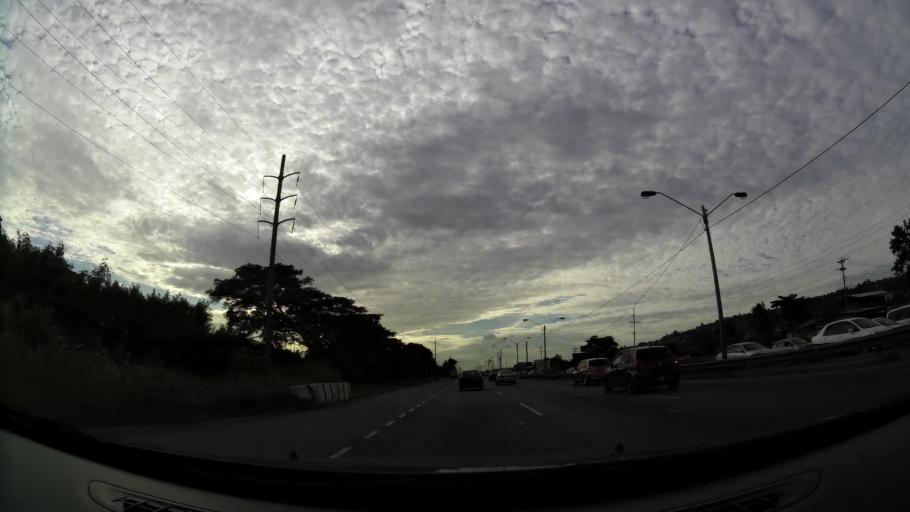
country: TT
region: San Juan/Laventille
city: Laventille
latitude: 10.6447
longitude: -61.4799
